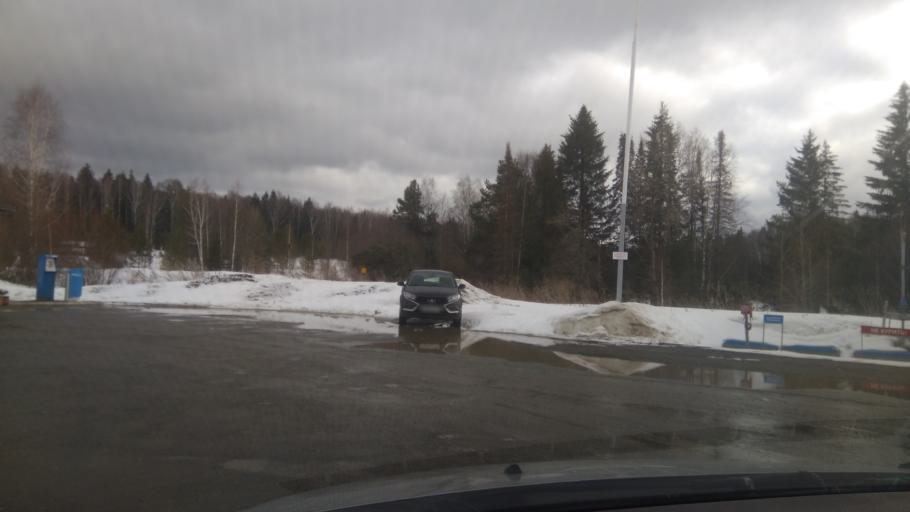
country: RU
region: Sverdlovsk
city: Bisert'
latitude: 56.8293
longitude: 59.0416
